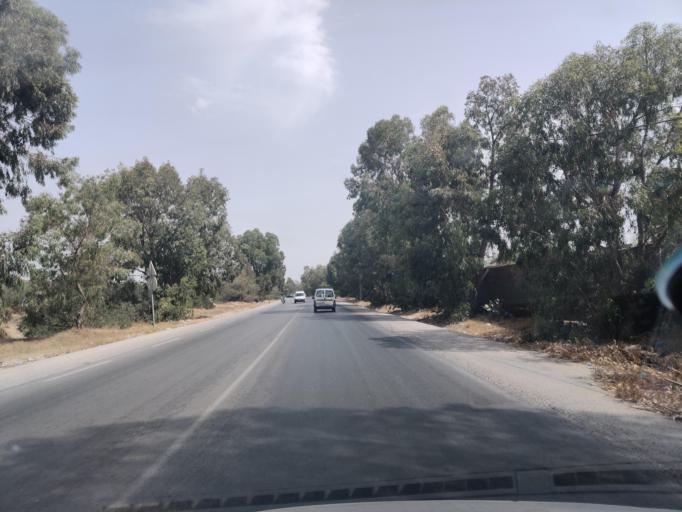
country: TN
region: Nabul
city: Al Hammamat
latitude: 36.4362
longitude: 10.5730
